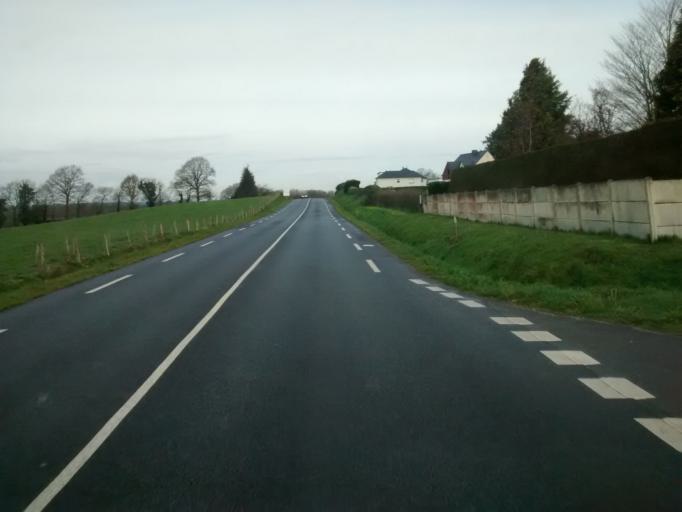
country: FR
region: Brittany
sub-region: Departement du Morbihan
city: Malestroit
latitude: 47.8298
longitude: -2.3849
